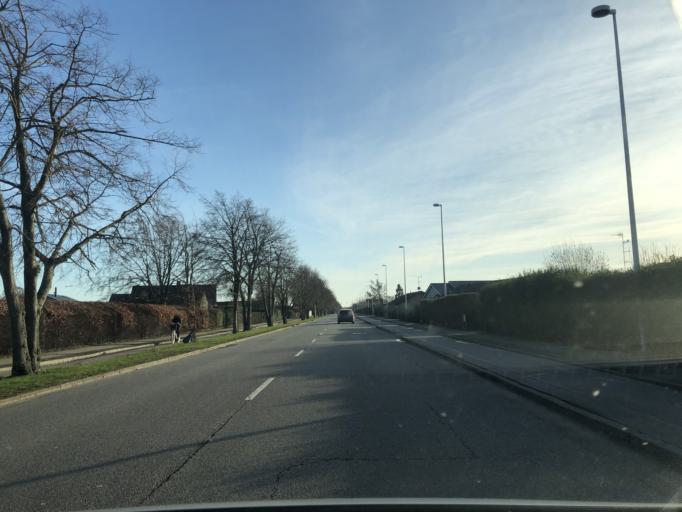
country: DK
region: Capital Region
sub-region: Tarnby Kommune
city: Tarnby
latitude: 55.6204
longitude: 12.5923
